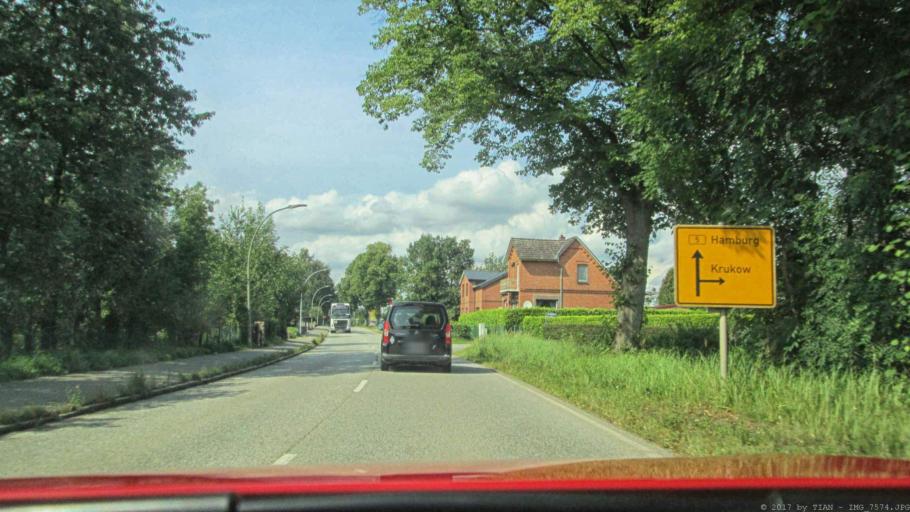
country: DE
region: Schleswig-Holstein
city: Wiershop
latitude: 53.4069
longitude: 10.4471
